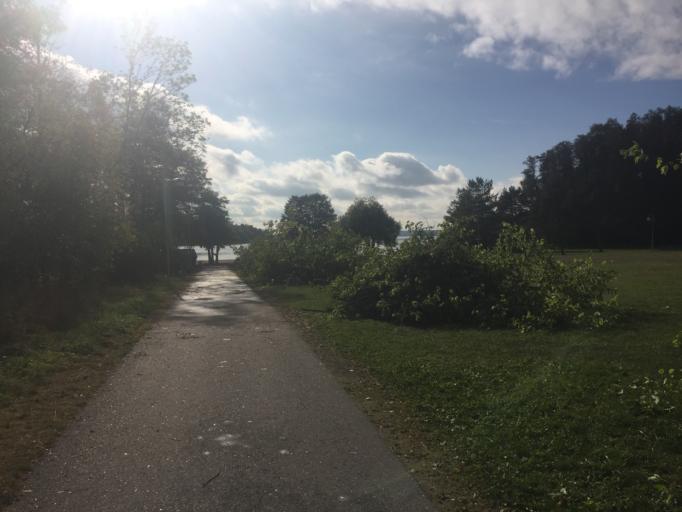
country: SE
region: Stockholm
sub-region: Taby Kommun
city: Taby
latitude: 59.4434
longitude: 18.1298
